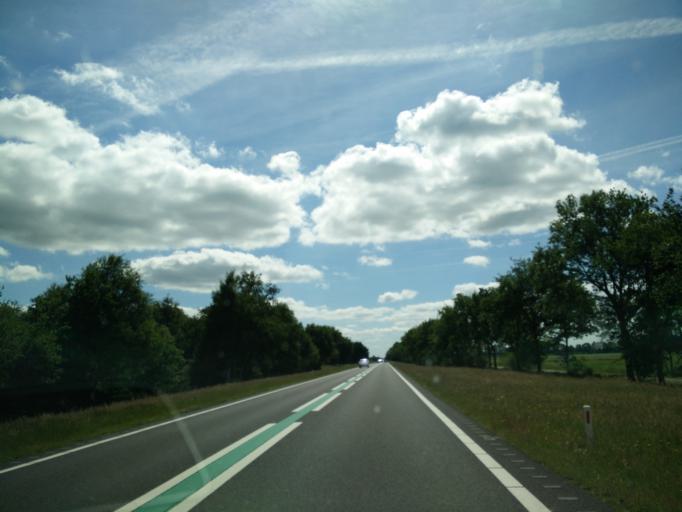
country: NL
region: Drenthe
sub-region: Gemeente Assen
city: Assen
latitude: 52.8509
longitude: 6.5670
